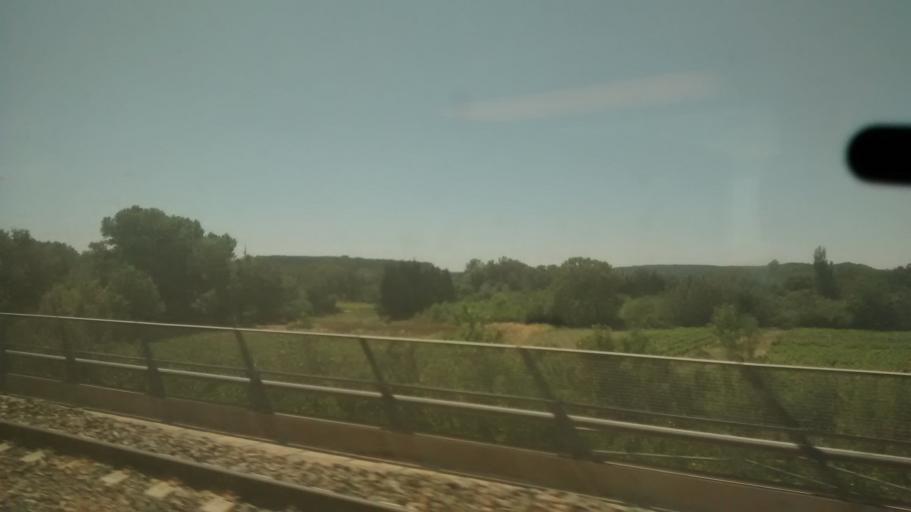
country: FR
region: Languedoc-Roussillon
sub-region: Departement du Gard
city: Pujaut
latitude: 44.0039
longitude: 4.7367
